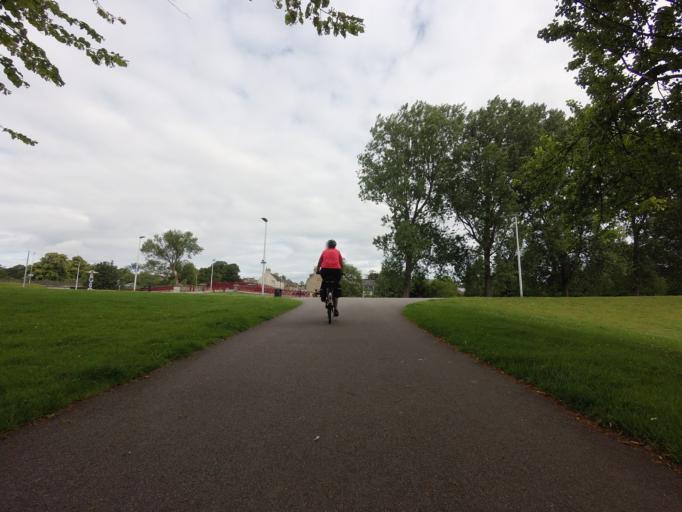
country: GB
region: Scotland
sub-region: Moray
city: Elgin
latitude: 57.6521
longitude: -3.3148
